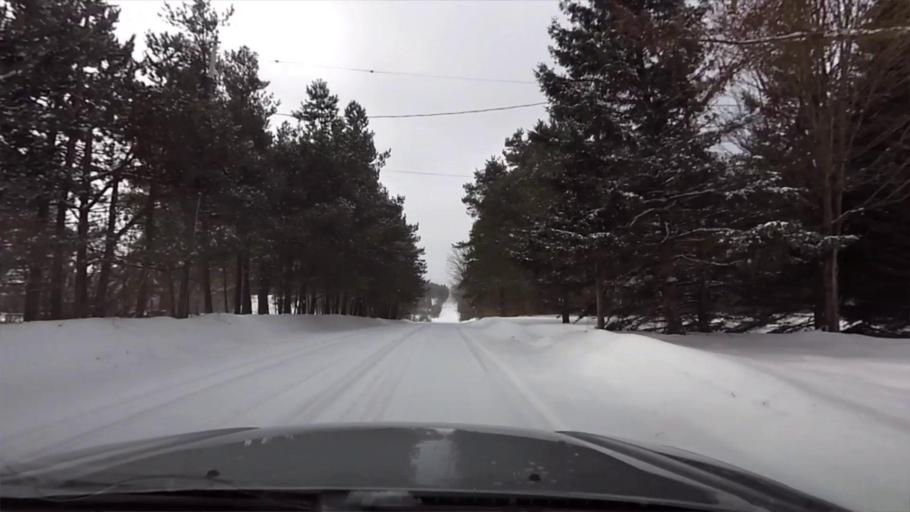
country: US
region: New York
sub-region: Cattaraugus County
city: Franklinville
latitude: 42.3311
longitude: -78.3540
